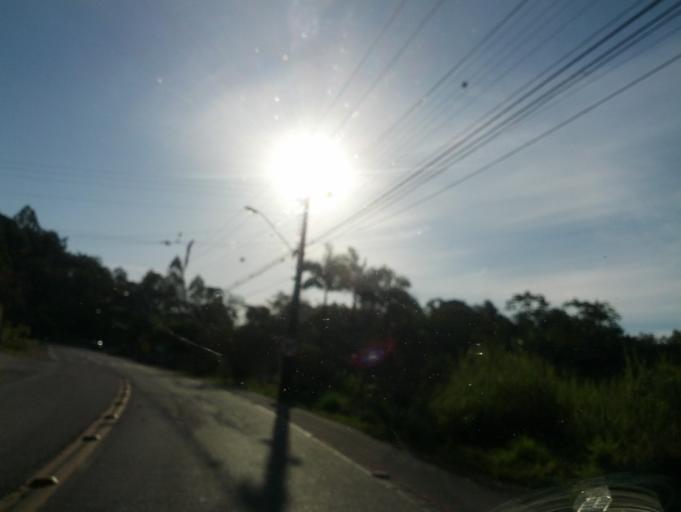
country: BR
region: Santa Catarina
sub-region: Indaial
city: Indaial
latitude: -26.8837
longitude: -49.1741
